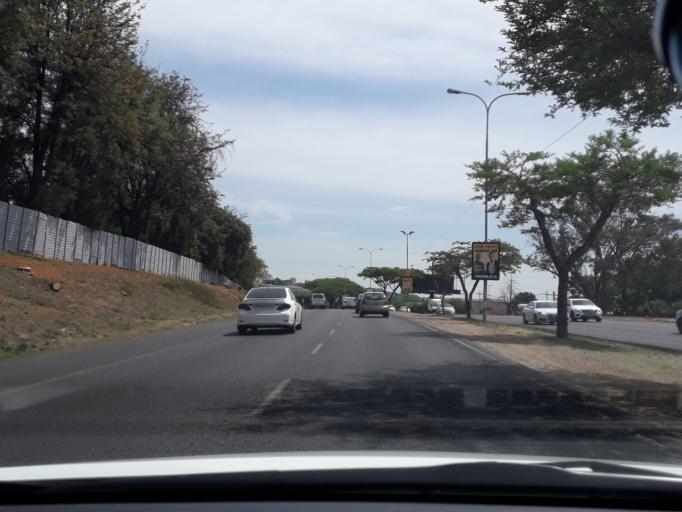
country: ZA
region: Gauteng
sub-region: City of Johannesburg Metropolitan Municipality
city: Johannesburg
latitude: -26.0739
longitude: 28.0266
